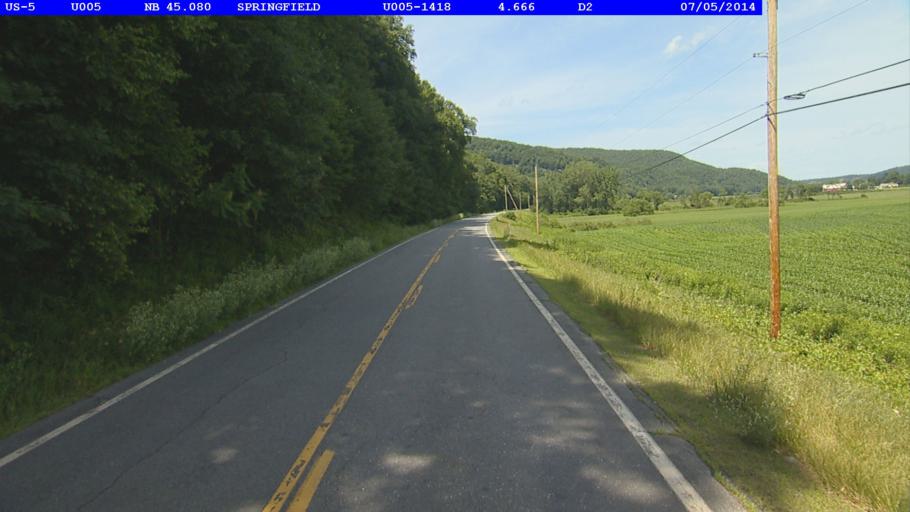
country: US
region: New Hampshire
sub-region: Sullivan County
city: Charlestown
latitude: 43.2810
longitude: -72.4136
